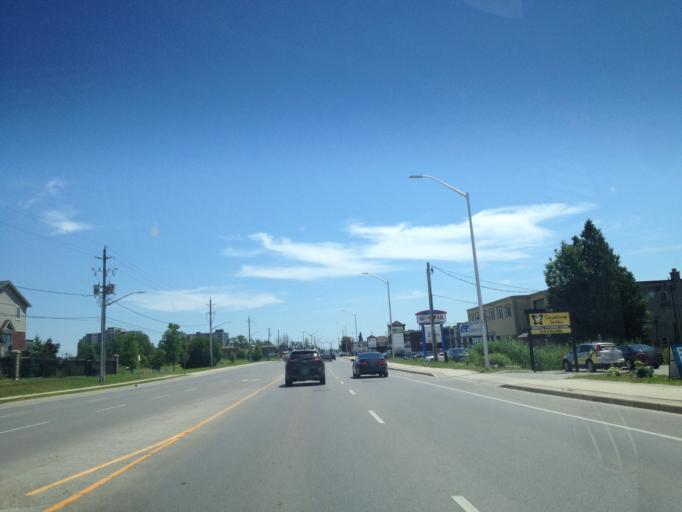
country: CA
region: Ontario
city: London
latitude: 43.0028
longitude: -81.3342
